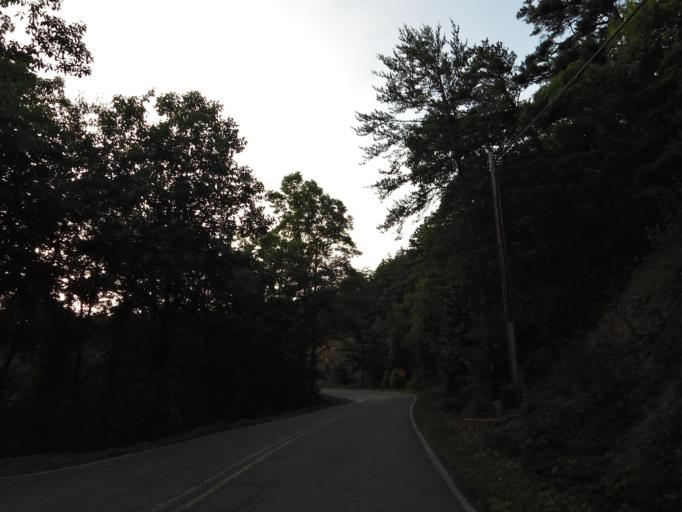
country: US
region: Tennessee
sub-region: Blount County
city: Maryville
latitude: 35.6299
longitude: -83.9442
